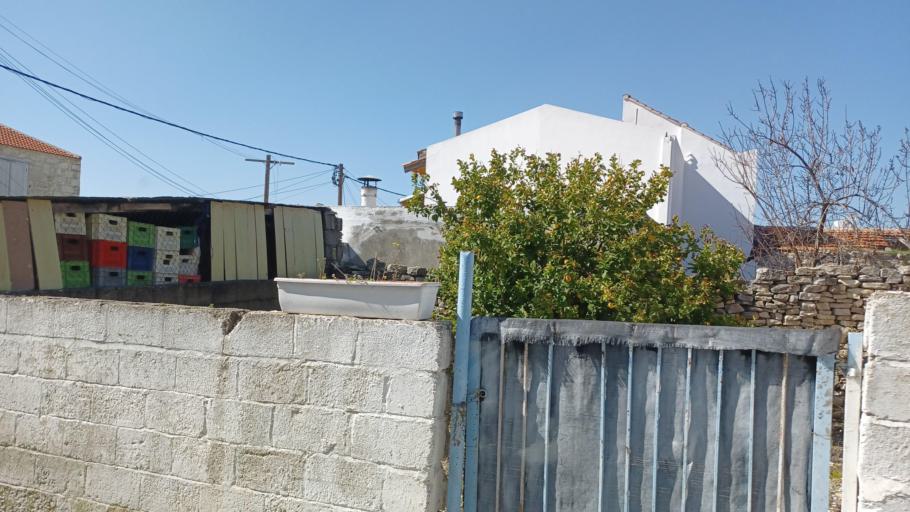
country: CY
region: Limassol
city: Pelendri
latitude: 34.8246
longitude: 32.9205
